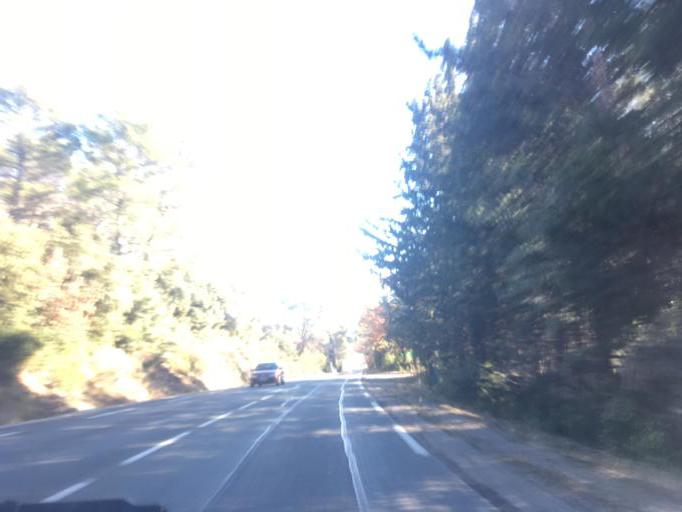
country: FR
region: Provence-Alpes-Cote d'Azur
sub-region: Departement du Var
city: Flayosc
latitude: 43.5418
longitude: 6.3694
